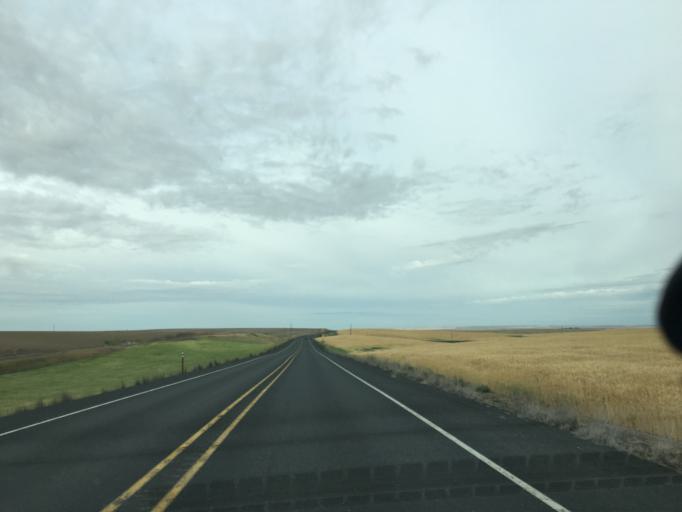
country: US
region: Washington
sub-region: Okanogan County
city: Coulee Dam
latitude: 47.7585
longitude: -118.6065
